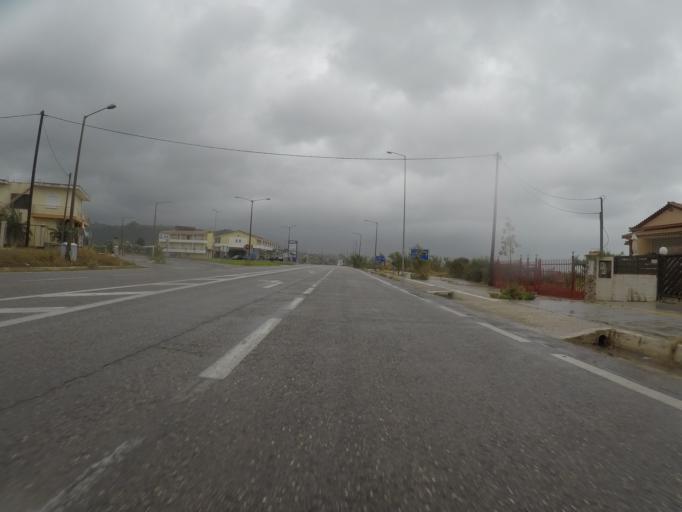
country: GR
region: Peloponnese
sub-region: Nomos Messinias
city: Kyparissia
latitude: 37.2980
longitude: 21.7024
